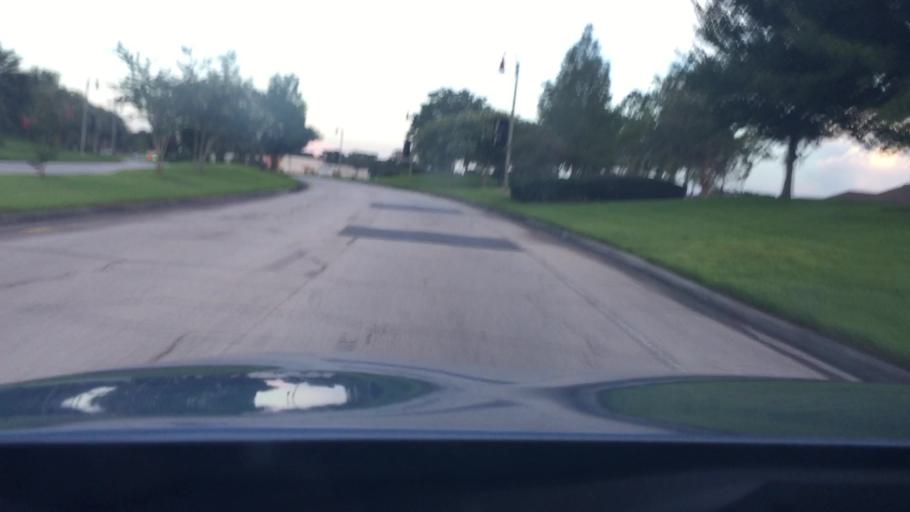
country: US
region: Florida
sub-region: Osceola County
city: Saint Cloud
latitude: 28.2248
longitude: -81.2981
